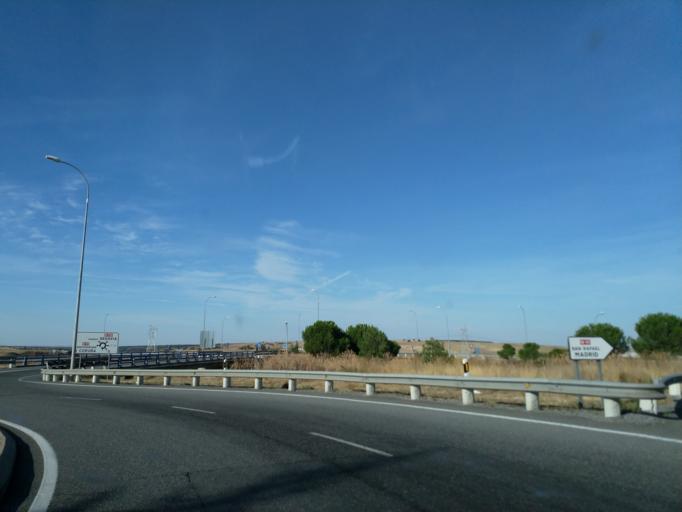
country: ES
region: Castille and Leon
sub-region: Provincia de Segovia
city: Villacastin
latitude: 40.7826
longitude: -4.4208
